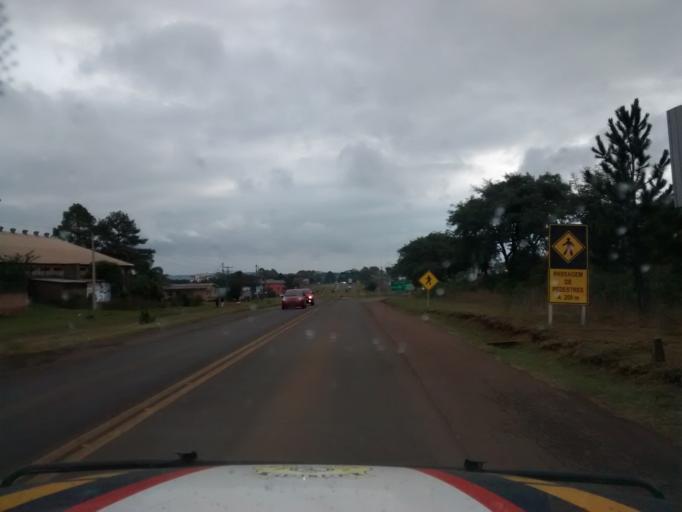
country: BR
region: Rio Grande do Sul
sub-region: Lagoa Vermelha
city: Lagoa Vermelha
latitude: -28.2055
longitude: -51.5194
